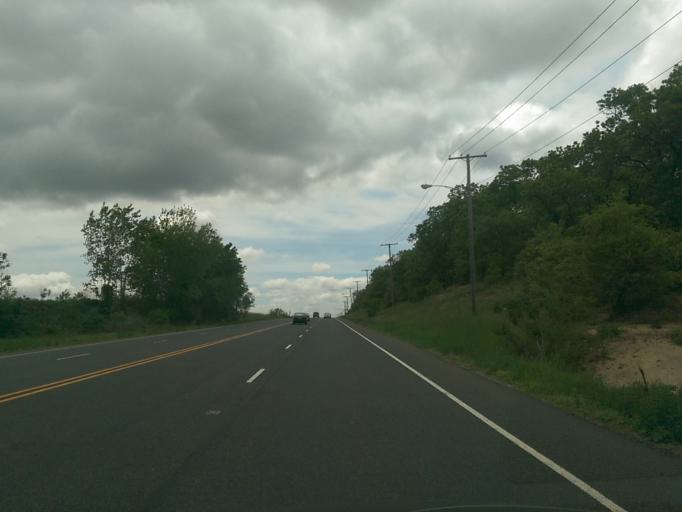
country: US
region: Indiana
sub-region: Lake County
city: Lake Station
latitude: 41.5948
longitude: -87.2314
